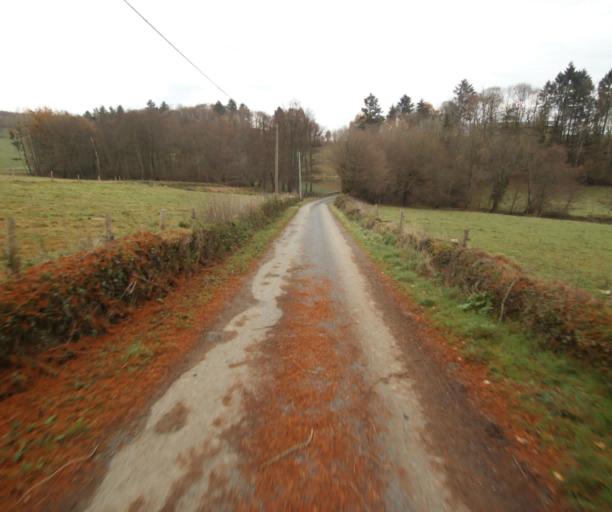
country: FR
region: Limousin
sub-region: Departement de la Correze
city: Laguenne
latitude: 45.2365
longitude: 1.7502
